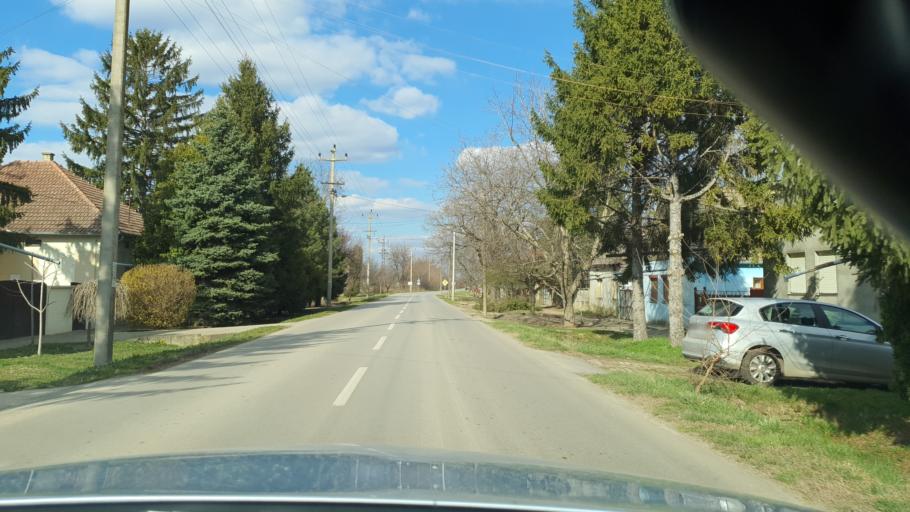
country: RS
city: Kulpin
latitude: 45.4075
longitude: 19.5902
